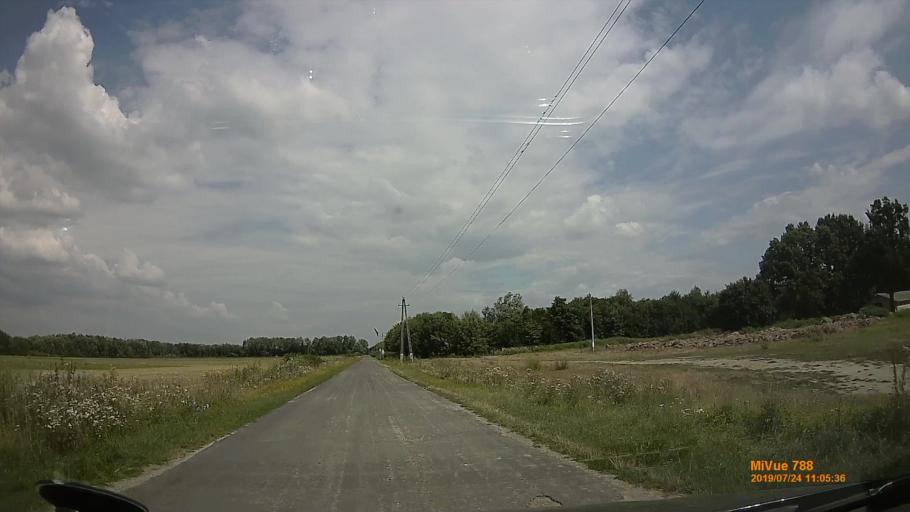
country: HU
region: Szabolcs-Szatmar-Bereg
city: Tarpa
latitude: 48.1808
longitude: 22.5189
